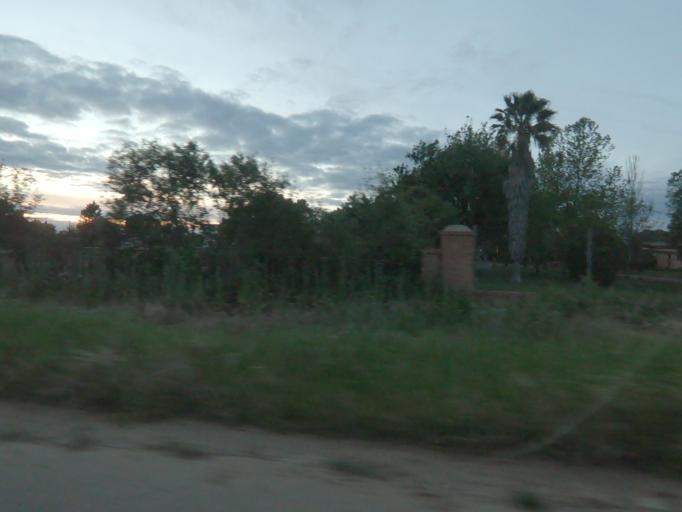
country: ES
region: Extremadura
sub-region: Provincia de Badajoz
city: Badajoz
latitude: 38.9299
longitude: -6.9298
